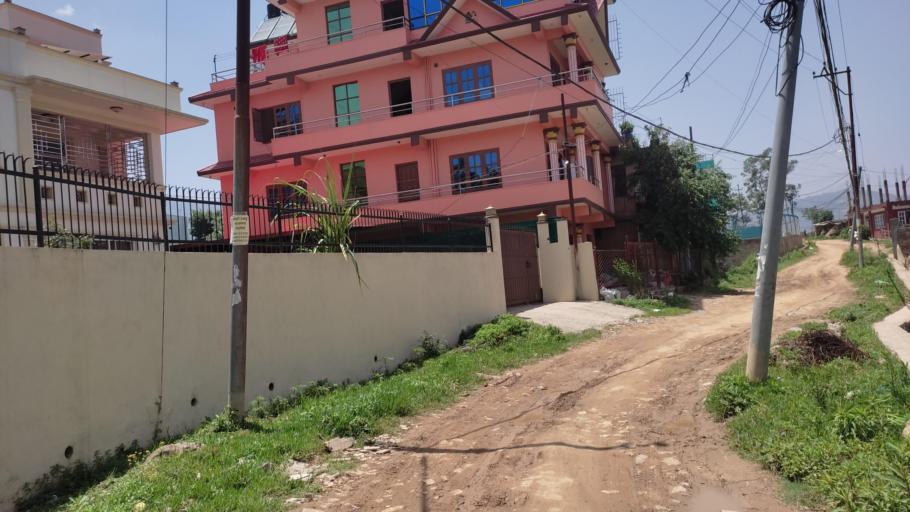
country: NP
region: Central Region
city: Kirtipur
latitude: 27.6694
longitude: 85.2626
